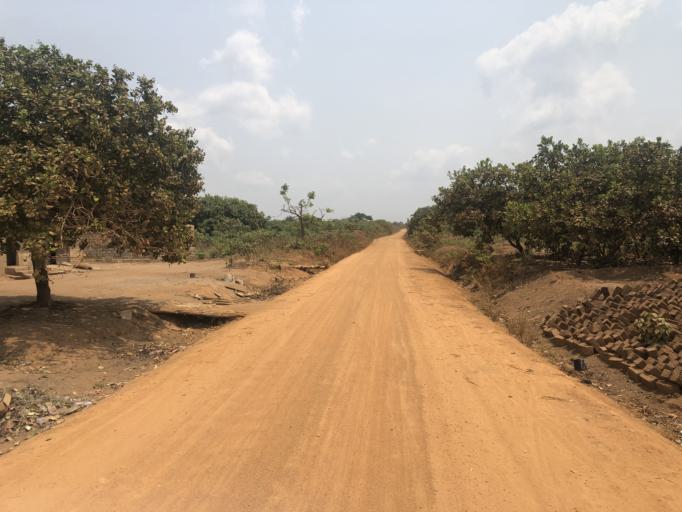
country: NG
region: Osun
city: Bode Osi
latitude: 7.8017
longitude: 4.1666
